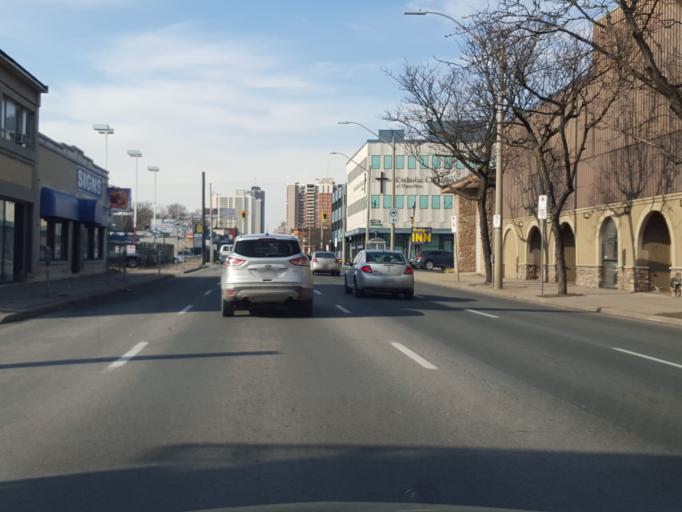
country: CA
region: Ontario
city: Hamilton
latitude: 43.2516
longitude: -79.8451
